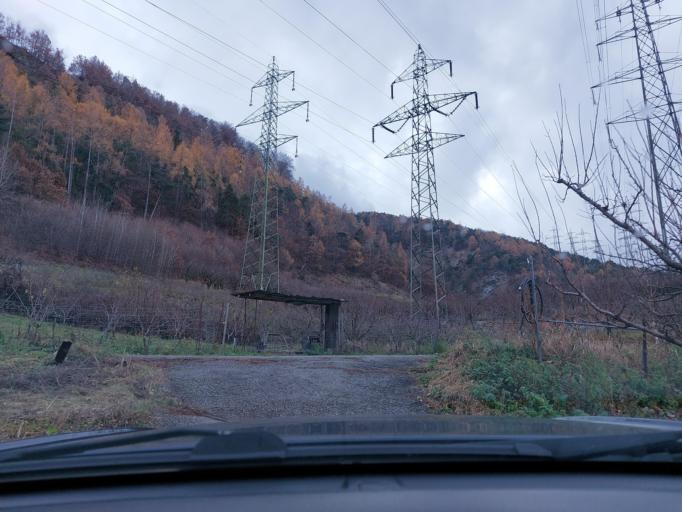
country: CH
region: Valais
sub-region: Martigny District
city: Saxon
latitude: 46.1430
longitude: 7.1810
